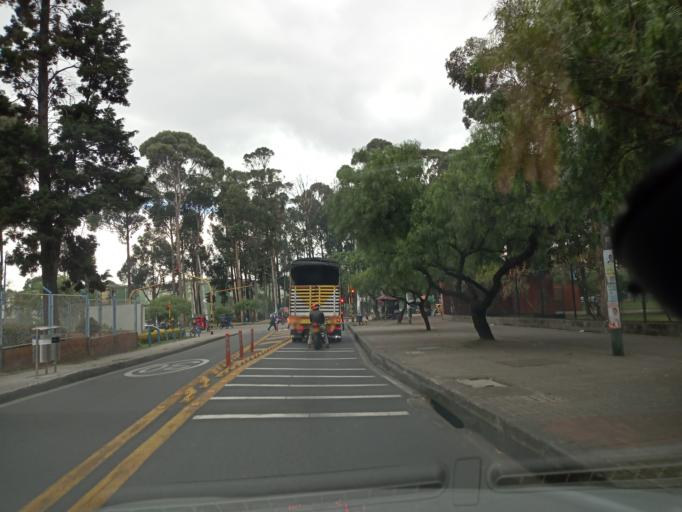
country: CO
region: Bogota D.C.
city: Bogota
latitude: 4.5721
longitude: -74.1056
